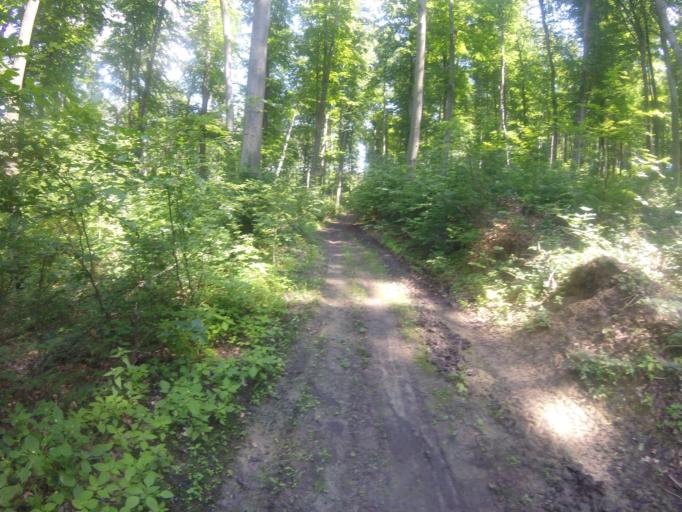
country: HU
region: Veszprem
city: Cseteny
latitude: 47.2609
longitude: 18.0056
